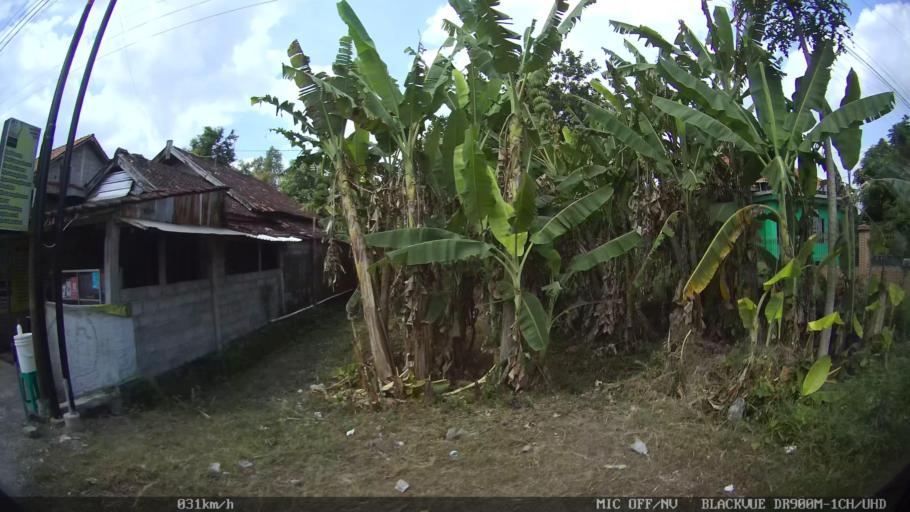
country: ID
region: Daerah Istimewa Yogyakarta
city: Kasihan
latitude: -7.8168
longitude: 110.3325
